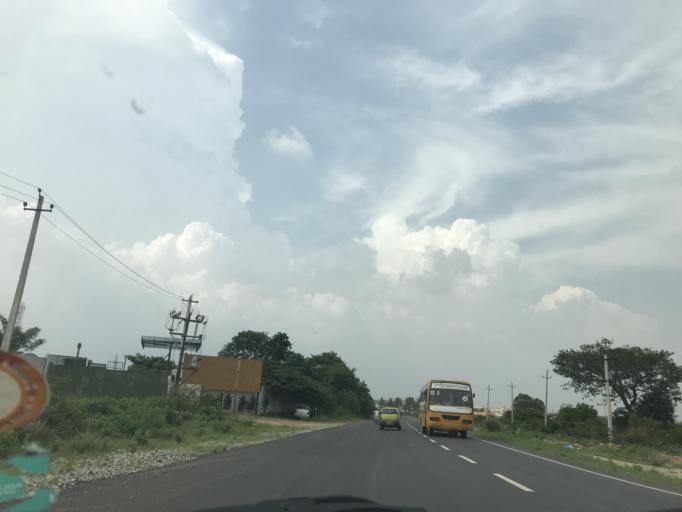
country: IN
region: Karnataka
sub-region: Bangalore Rural
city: Devanhalli
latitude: 13.1676
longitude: 77.6882
